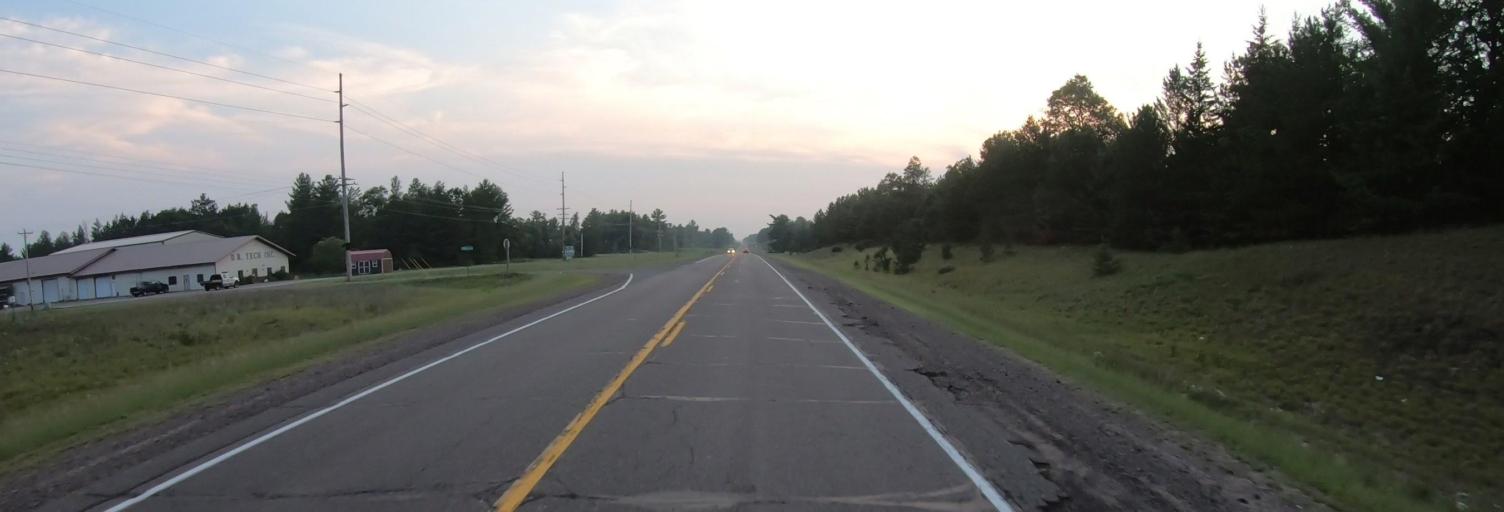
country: US
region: Wisconsin
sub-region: Burnett County
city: Grantsburg
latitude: 45.7731
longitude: -92.7171
